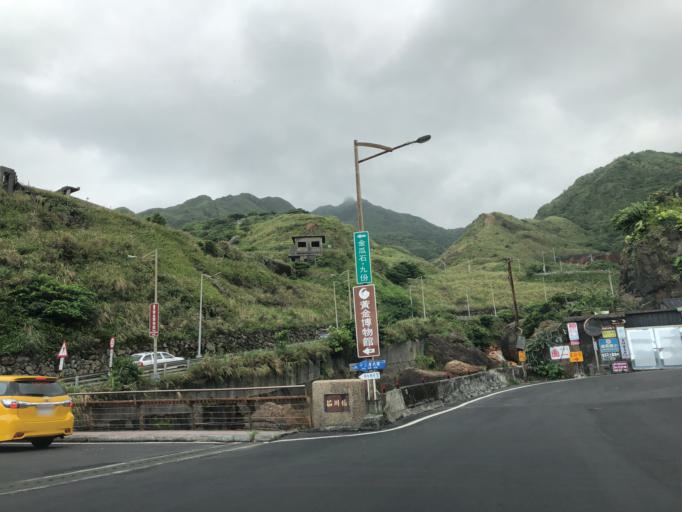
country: TW
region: Taiwan
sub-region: Keelung
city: Keelung
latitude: 25.1198
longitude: 121.8618
